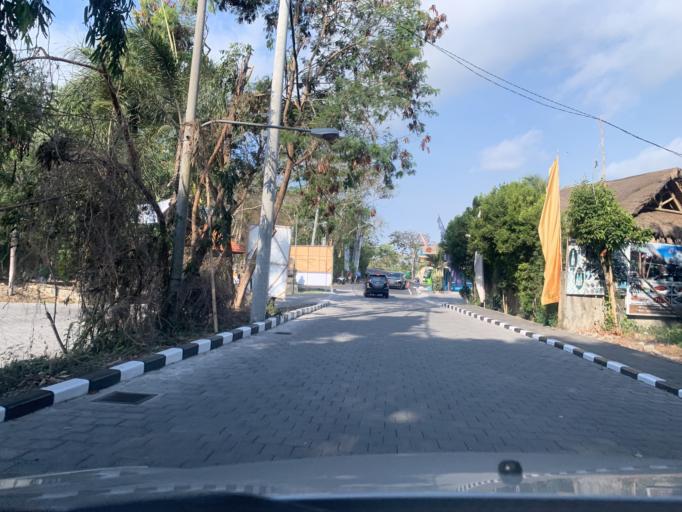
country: ID
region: Bali
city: Banjar Pangkungtibah Selatan
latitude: -8.6166
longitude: 115.0870
